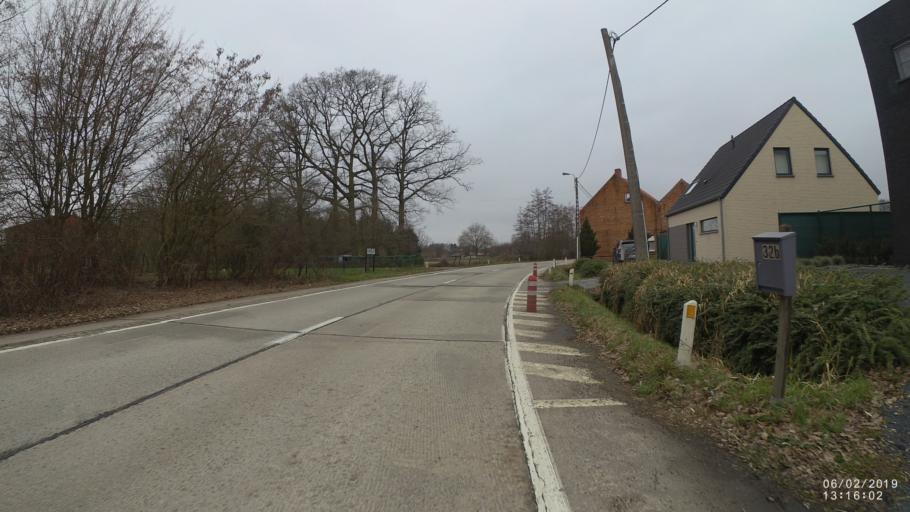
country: BE
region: Flanders
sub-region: Provincie Vlaams-Brabant
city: Aarschot
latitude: 51.0166
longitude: 4.8267
